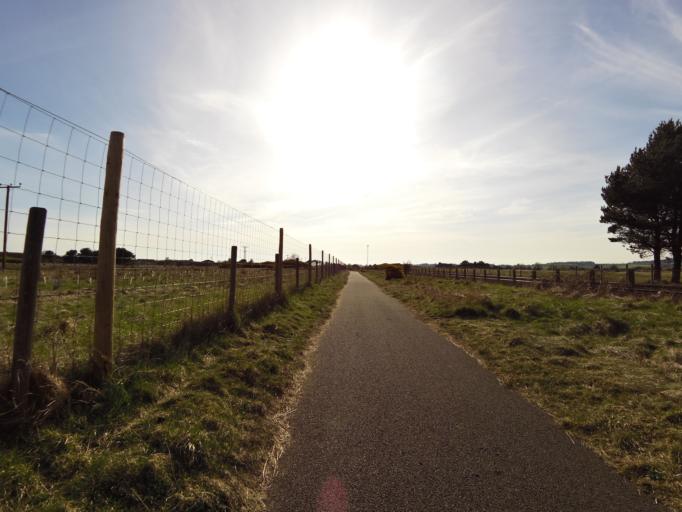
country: GB
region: Scotland
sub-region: Angus
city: Carnoustie
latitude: 56.4880
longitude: -2.7736
